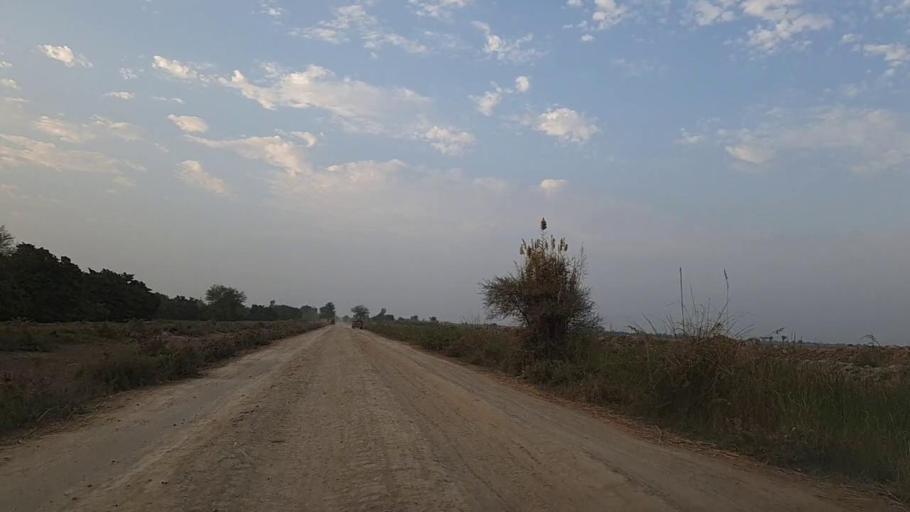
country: PK
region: Sindh
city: Mirwah Gorchani
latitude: 25.3302
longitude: 69.2137
